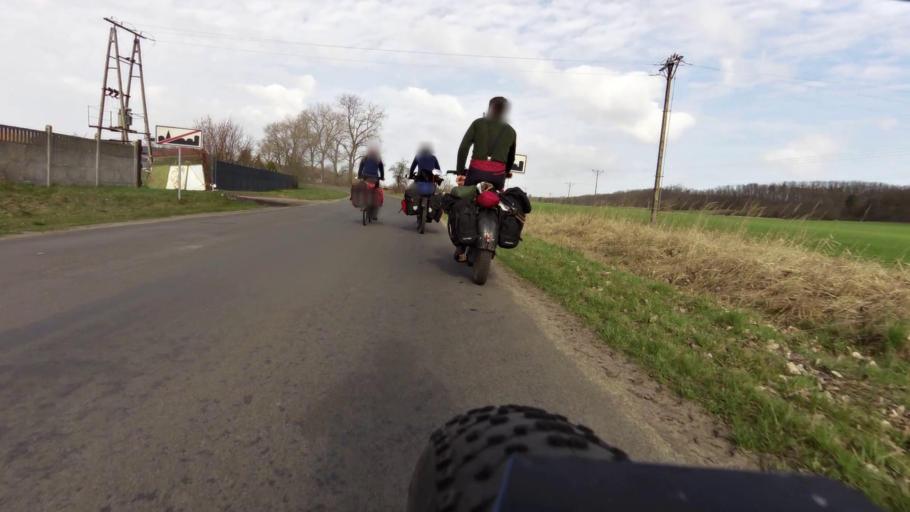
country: DE
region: Brandenburg
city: Brieskow-Finkenheerd
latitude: 52.3020
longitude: 14.5971
